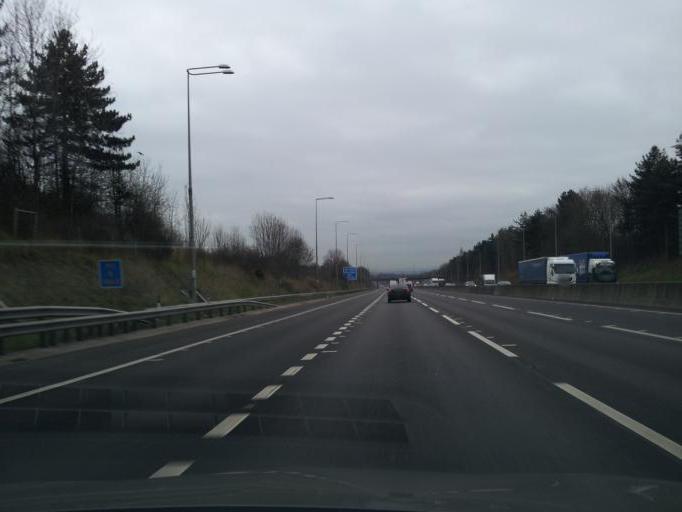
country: GB
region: England
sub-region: Derbyshire
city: Long Eaton
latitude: 52.9246
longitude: -1.3002
